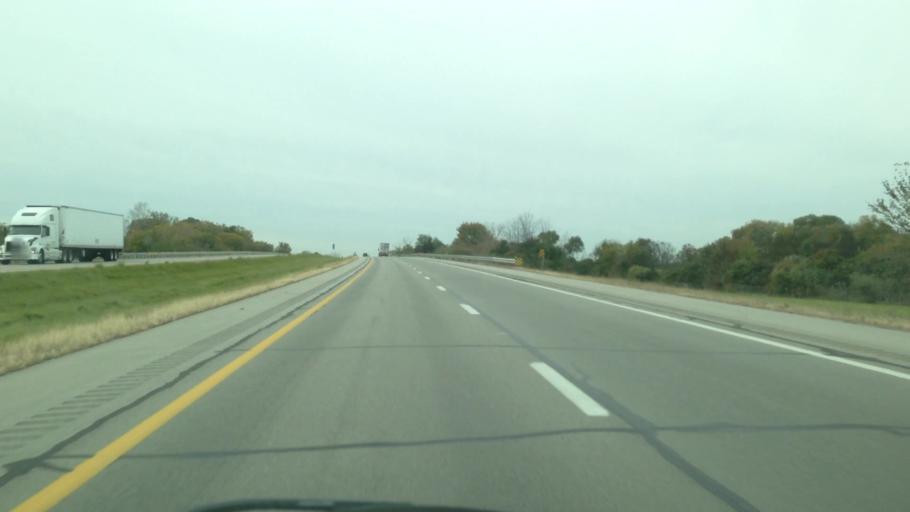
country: US
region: Ohio
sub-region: Lucas County
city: Holland
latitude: 41.5919
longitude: -83.7276
